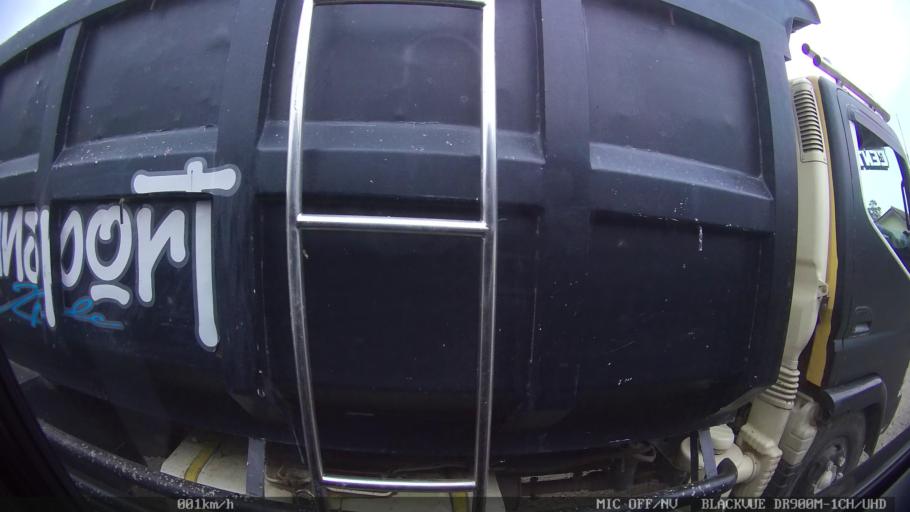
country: ID
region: Lampung
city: Gadingrejo
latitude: -5.3812
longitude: 105.0346
